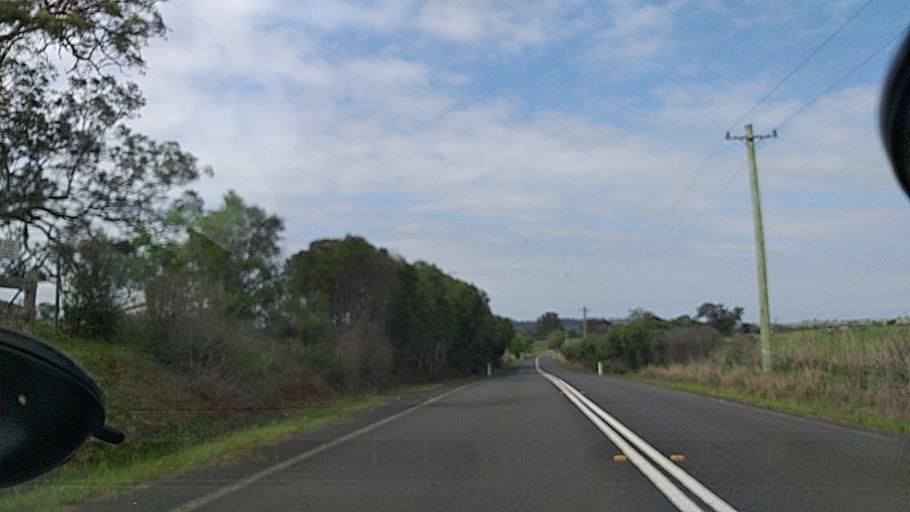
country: AU
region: New South Wales
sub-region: Camden
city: Camden South
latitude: -34.1256
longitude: 150.7242
